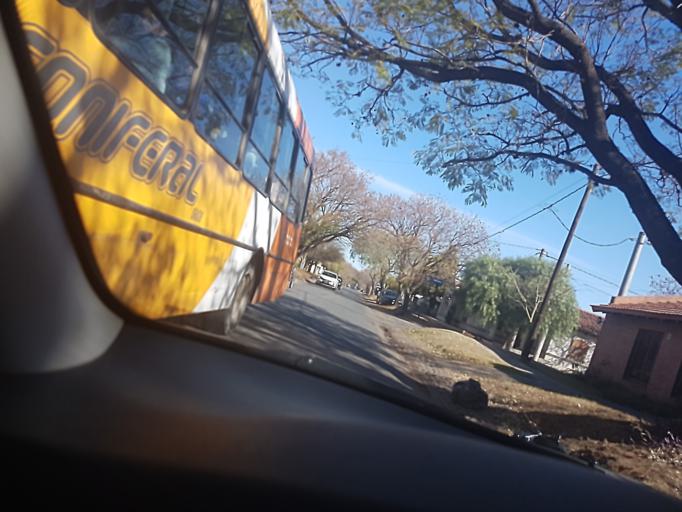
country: AR
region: Cordoba
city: Villa Allende
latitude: -31.3547
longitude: -64.2536
